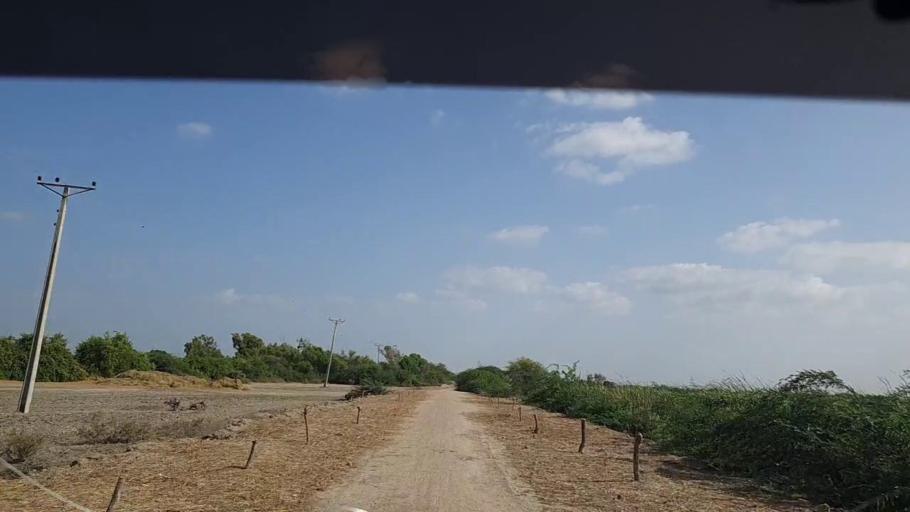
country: PK
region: Sindh
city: Kadhan
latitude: 24.4640
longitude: 68.8520
